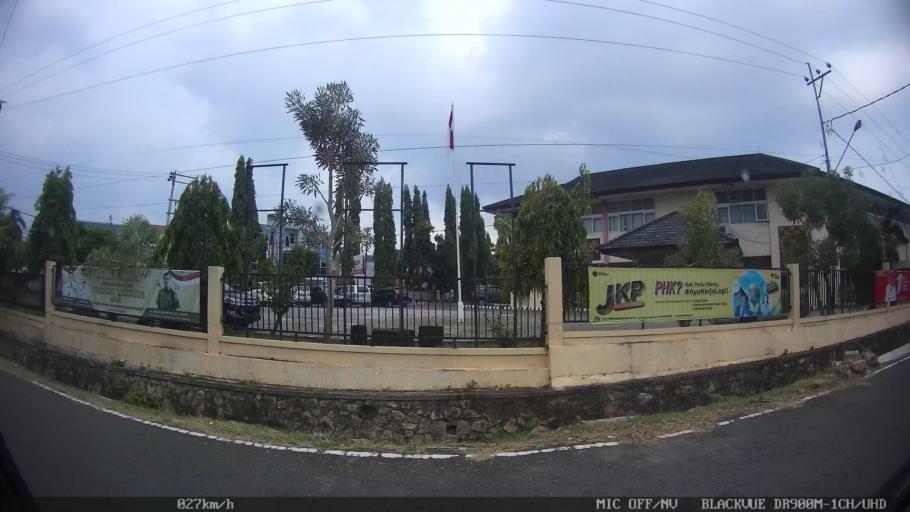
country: ID
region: Lampung
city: Bandarlampung
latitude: -5.4254
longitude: 105.2741
